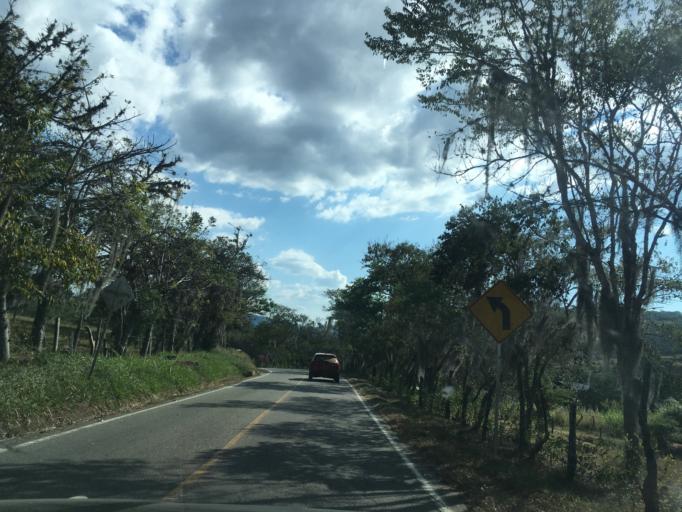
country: CO
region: Santander
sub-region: San Gil
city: San Gil
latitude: 6.5902
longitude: -73.1579
